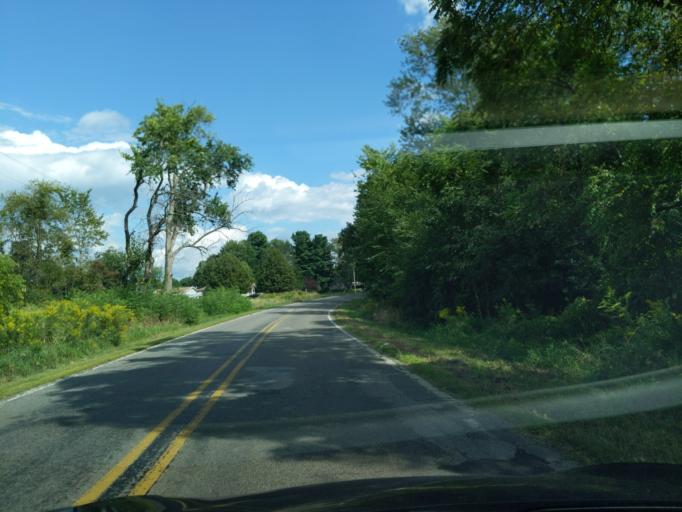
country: US
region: Michigan
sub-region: Jackson County
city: Jackson
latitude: 42.2884
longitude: -84.4683
